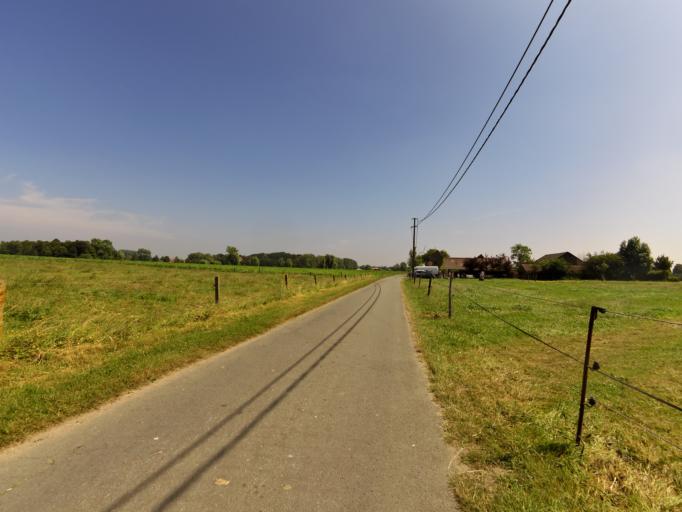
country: BE
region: Flanders
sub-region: Provincie West-Vlaanderen
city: Zedelgem
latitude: 51.1467
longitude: 3.1515
